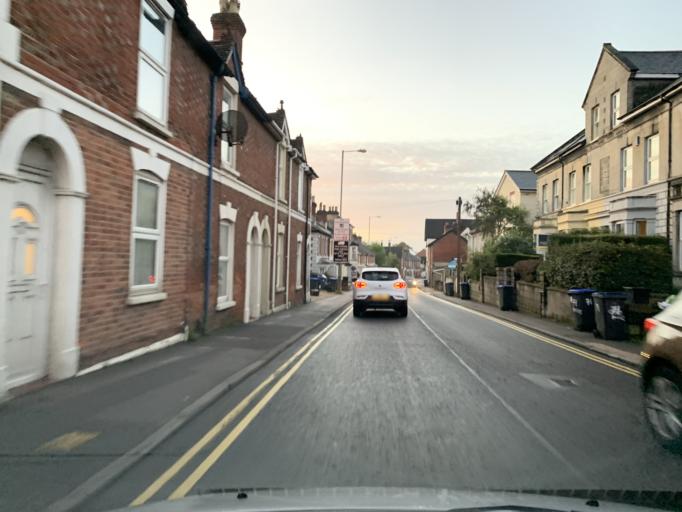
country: GB
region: England
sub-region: Wiltshire
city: Salisbury
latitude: 51.0750
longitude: -1.8075
